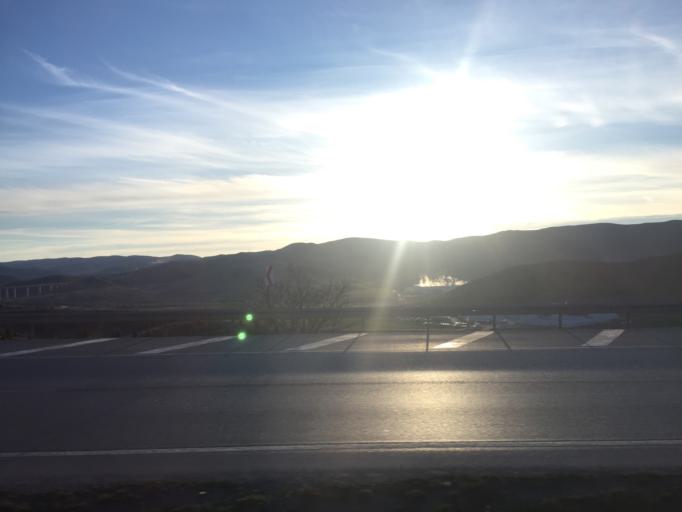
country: TR
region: Kirikkale
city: Yahsihan
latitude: 39.8881
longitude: 33.4318
